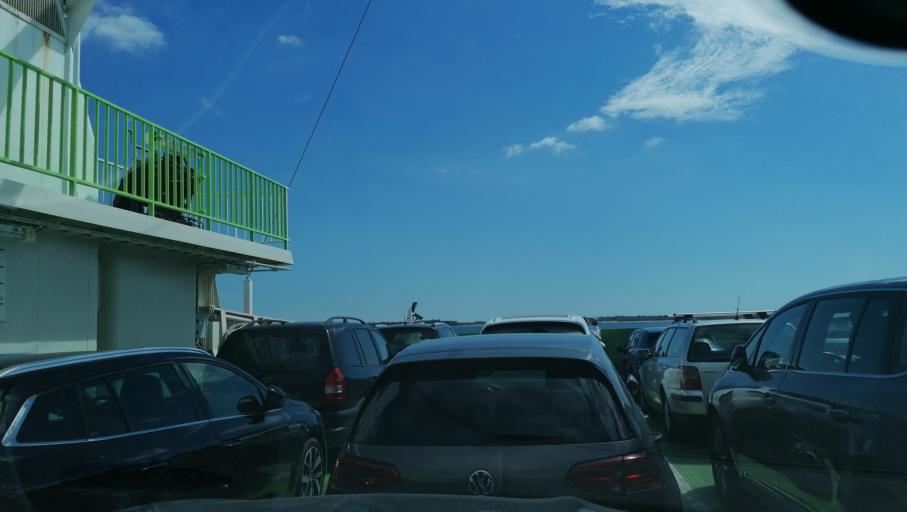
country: PT
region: Setubal
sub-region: Setubal
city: Setubal
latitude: 38.5084
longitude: -8.8848
